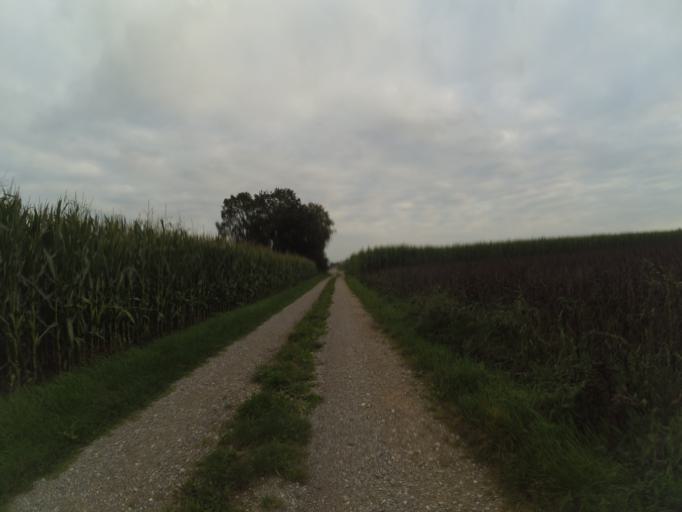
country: DE
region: Bavaria
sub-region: Swabia
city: Buchloe
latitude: 48.0514
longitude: 10.7412
